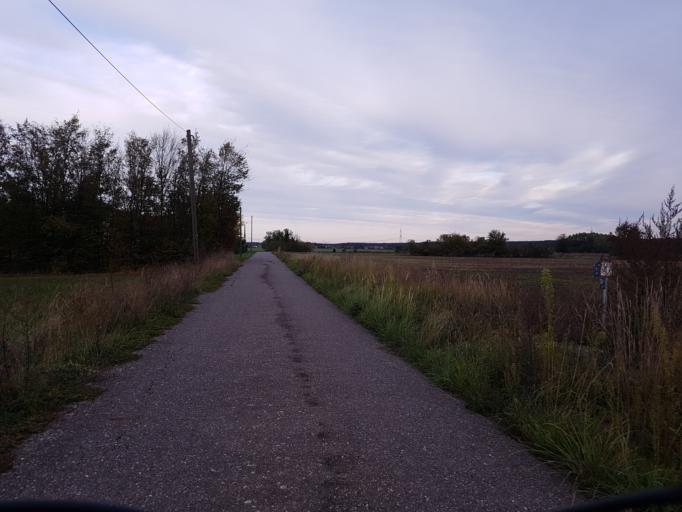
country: DE
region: Brandenburg
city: Schilda
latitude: 51.6311
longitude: 13.3517
